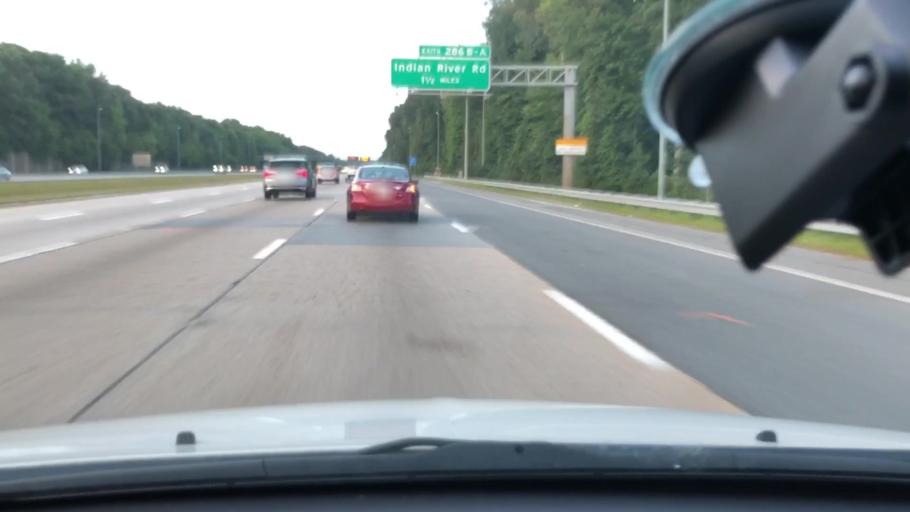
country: US
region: Virginia
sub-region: City of Chesapeake
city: Chesapeake
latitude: 36.7911
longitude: -76.2177
